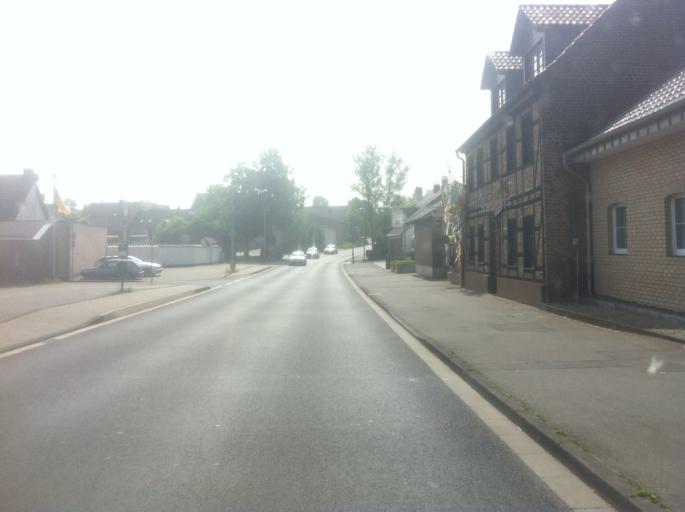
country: DE
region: North Rhine-Westphalia
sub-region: Regierungsbezirk Koln
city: Weilerswist
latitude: 50.7549
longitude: 6.7729
